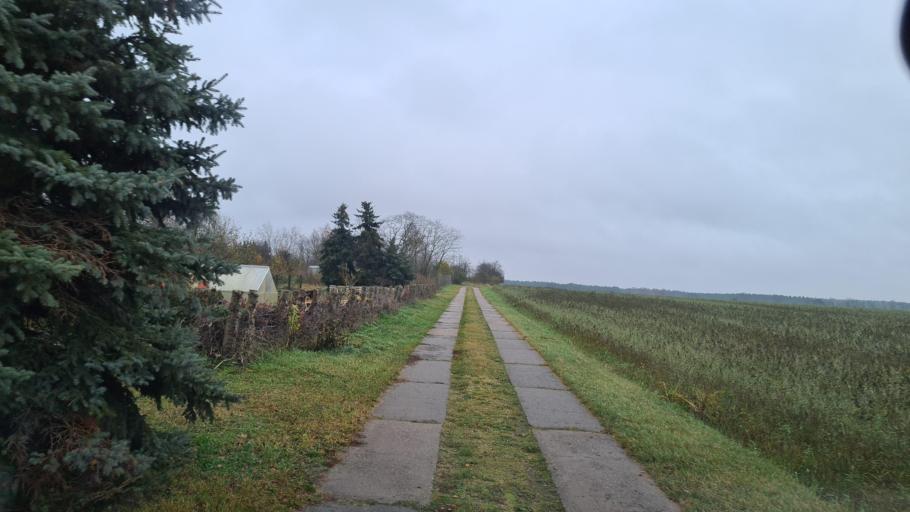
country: DE
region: Brandenburg
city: Retzow
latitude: 52.5783
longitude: 12.6257
